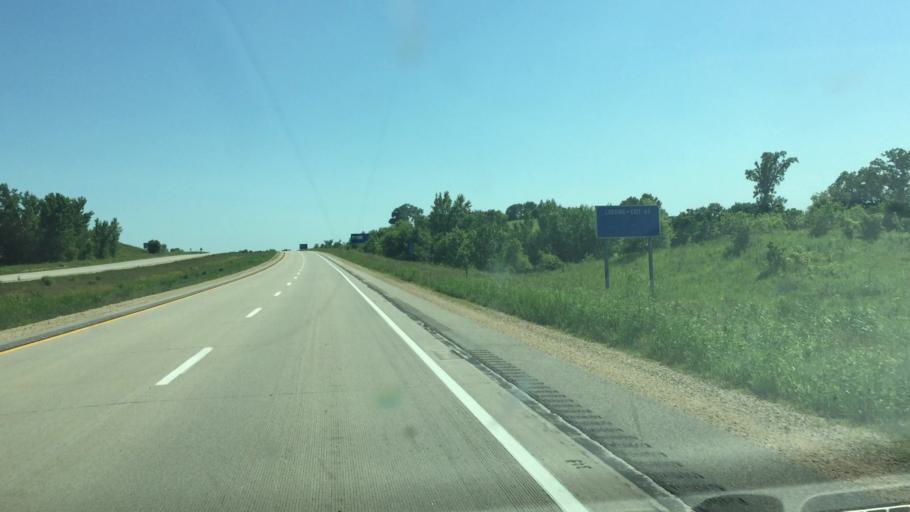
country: US
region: Iowa
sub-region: Jones County
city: Monticello
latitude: 42.2437
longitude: -91.1661
